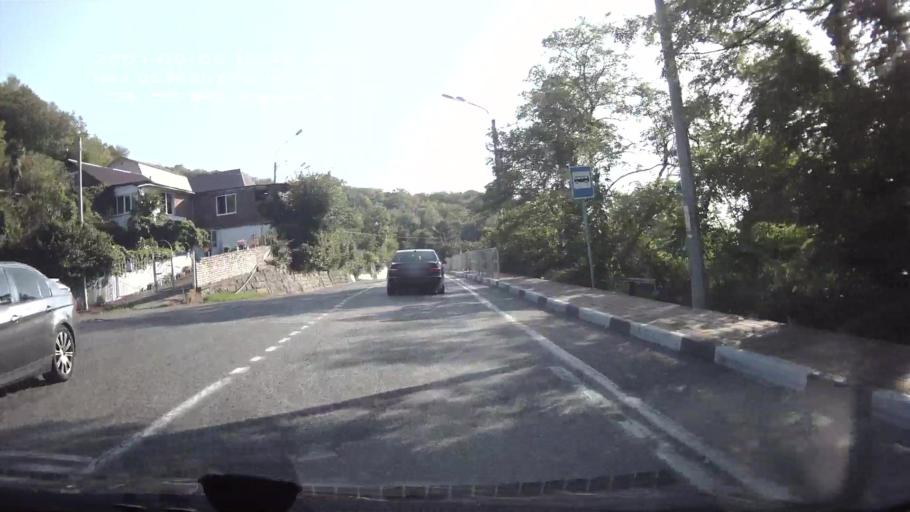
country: RU
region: Krasnodarskiy
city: Shepsi
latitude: 44.0576
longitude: 39.1346
